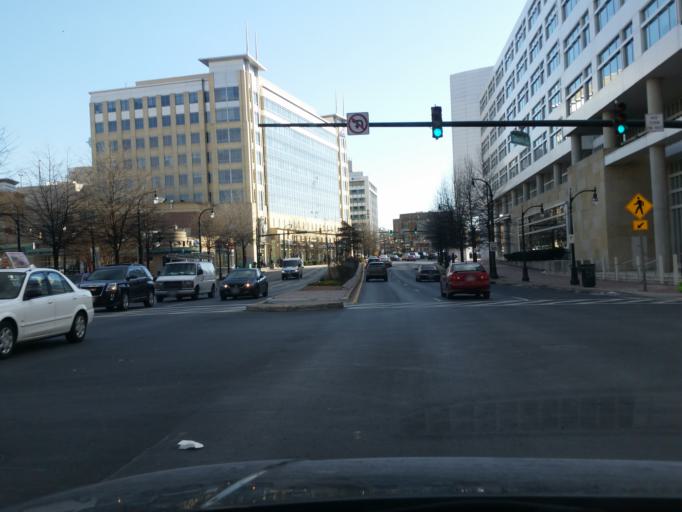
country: US
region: Maryland
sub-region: Montgomery County
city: Silver Spring
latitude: 38.9962
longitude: -77.0283
